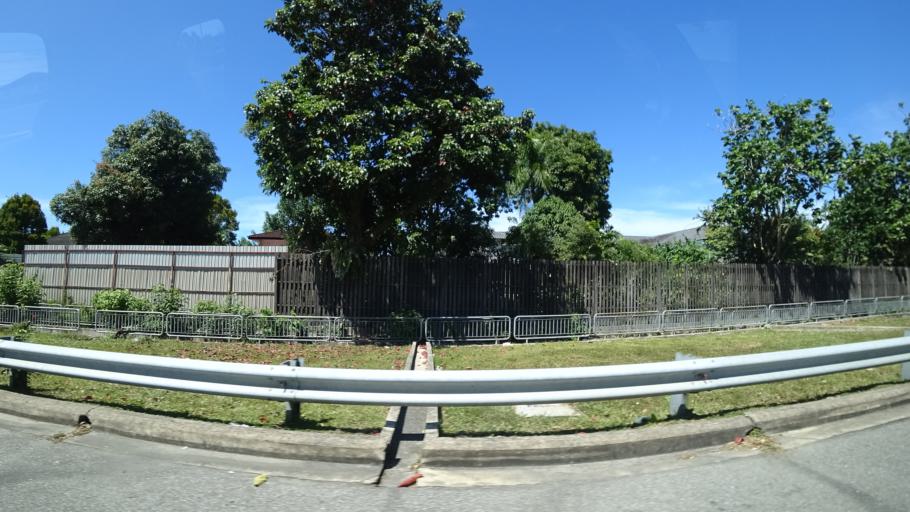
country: BN
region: Brunei and Muara
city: Bandar Seri Begawan
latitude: 4.9160
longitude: 114.9203
